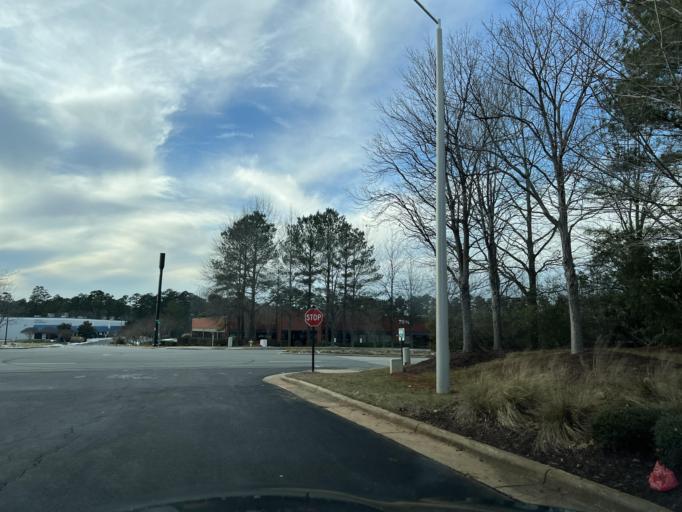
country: US
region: North Carolina
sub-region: Wake County
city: Raleigh
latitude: 35.8715
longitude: -78.5895
